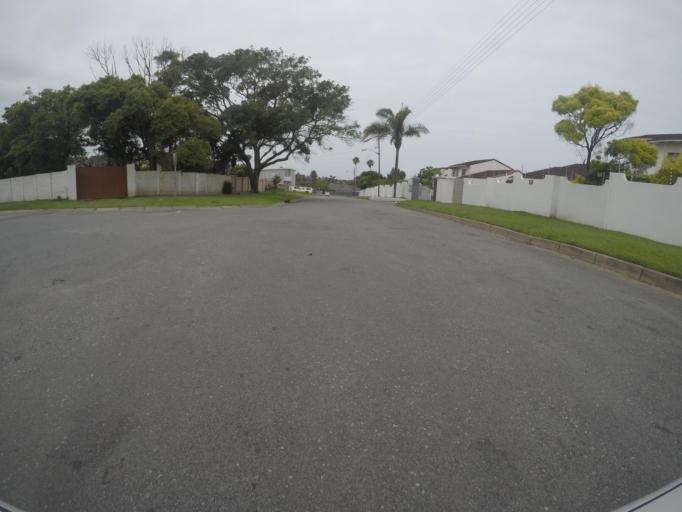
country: ZA
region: Eastern Cape
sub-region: Buffalo City Metropolitan Municipality
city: East London
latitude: -32.9738
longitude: 27.9400
